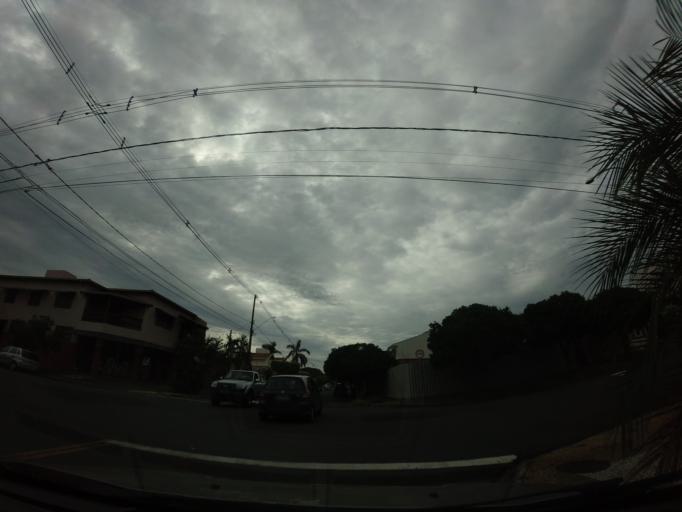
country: BR
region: Sao Paulo
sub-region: Piracicaba
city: Piracicaba
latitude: -22.7119
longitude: -47.6662
